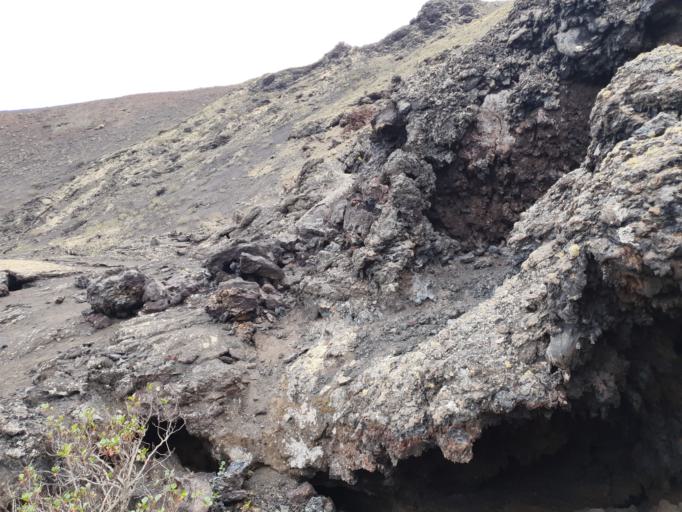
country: ES
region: Canary Islands
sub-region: Provincia de Las Palmas
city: Tinajo
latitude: 29.0104
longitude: -13.7186
